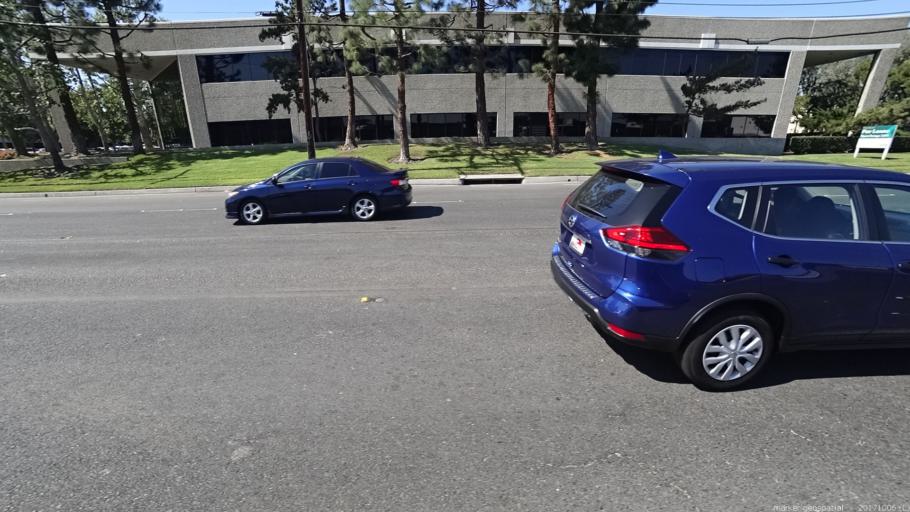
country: US
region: California
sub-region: Orange County
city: Stanton
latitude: 33.7987
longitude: -118.0016
